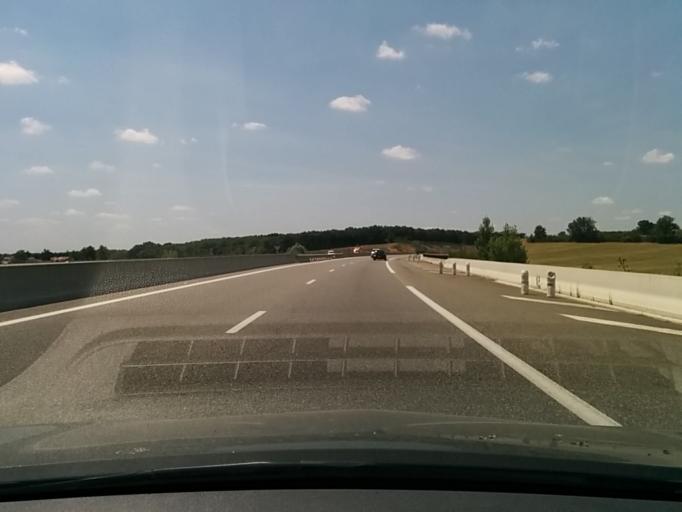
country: FR
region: Midi-Pyrenees
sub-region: Departement de la Haute-Garonne
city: La Salvetat-Saint-Gilles
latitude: 43.5870
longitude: 1.2693
